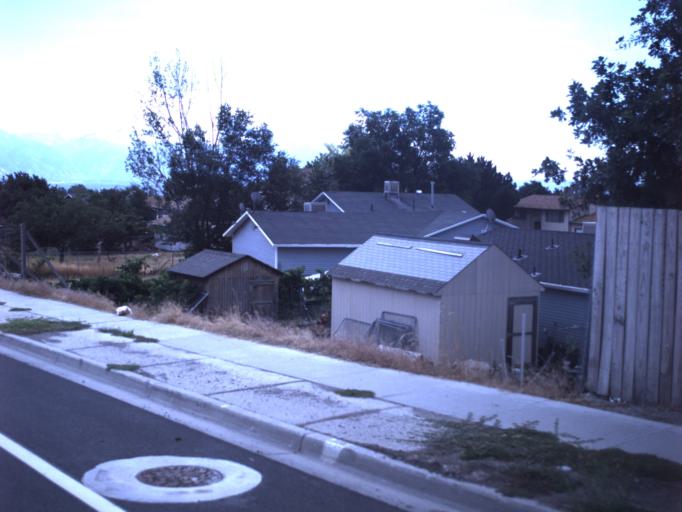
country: US
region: Utah
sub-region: Salt Lake County
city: Oquirrh
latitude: 40.6530
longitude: -112.0291
